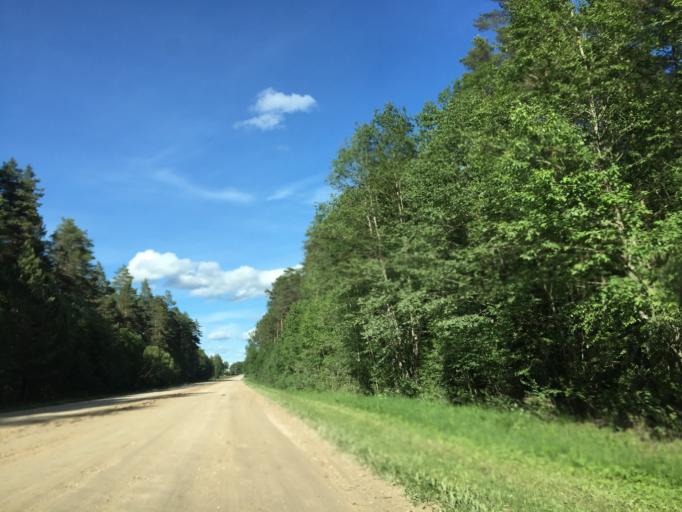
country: LV
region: Vecumnieki
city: Vecumnieki
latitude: 56.4471
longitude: 24.5833
